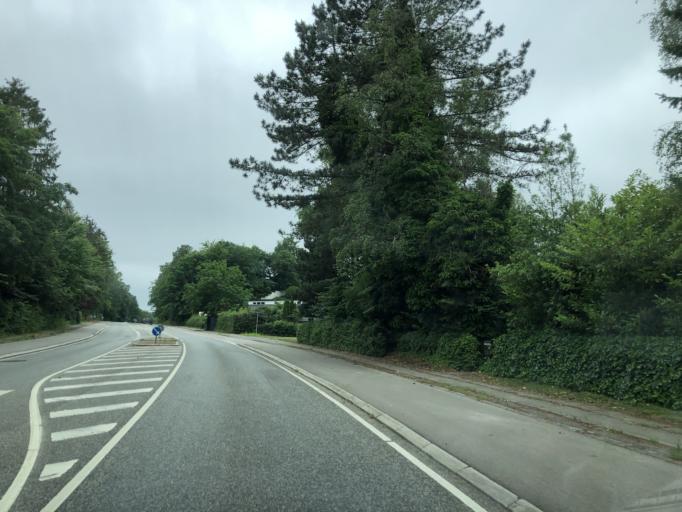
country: DK
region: Capital Region
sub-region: Rudersdal Kommune
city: Trorod
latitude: 55.8125
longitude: 12.5136
